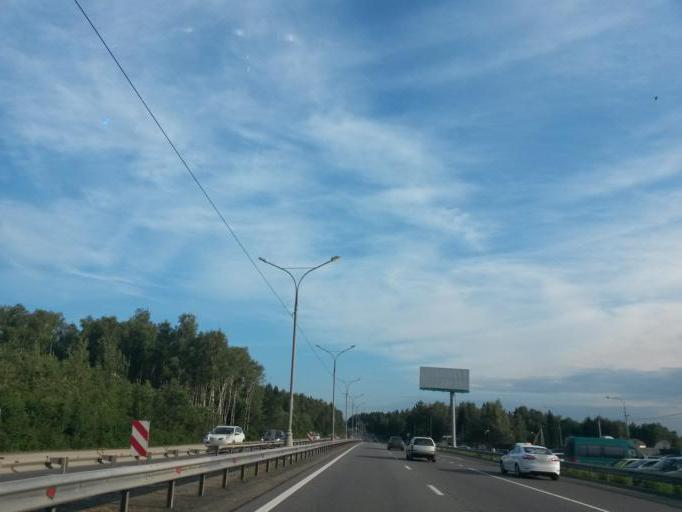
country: RU
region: Moskovskaya
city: Vostryakovo
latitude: 55.4658
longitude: 37.8538
